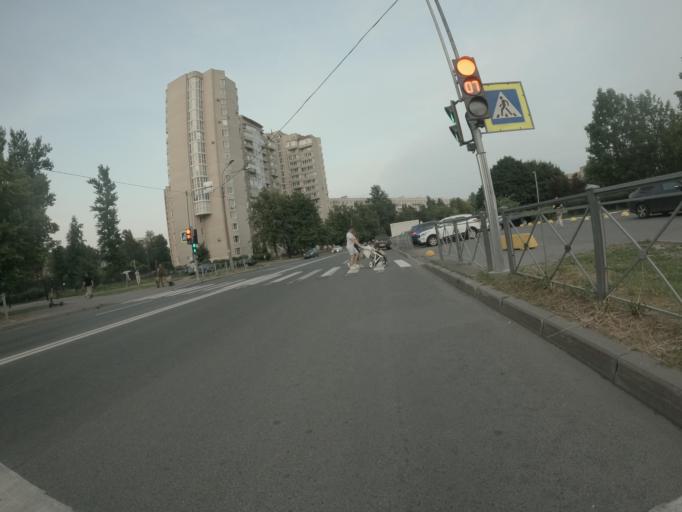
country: RU
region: St.-Petersburg
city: Krasnogvargeisky
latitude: 59.9668
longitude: 30.4297
